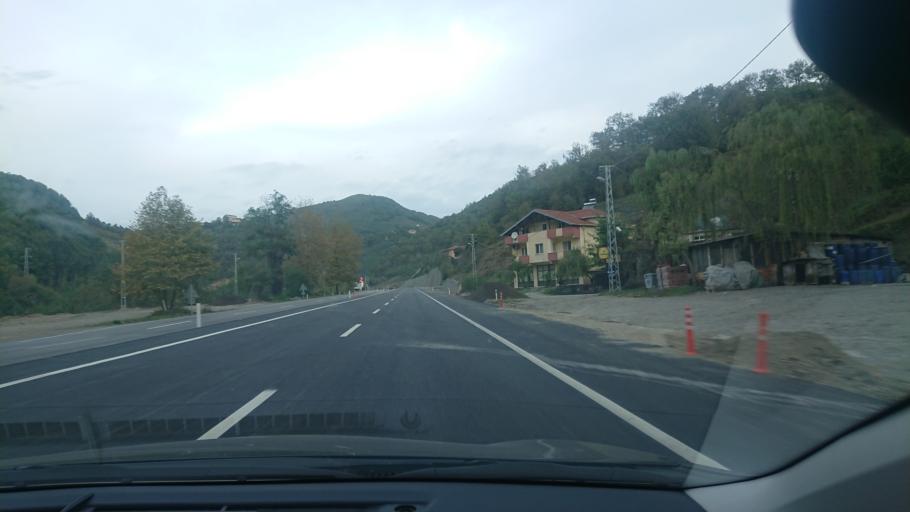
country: TR
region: Zonguldak
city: Beycuma
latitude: 41.3831
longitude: 31.9438
